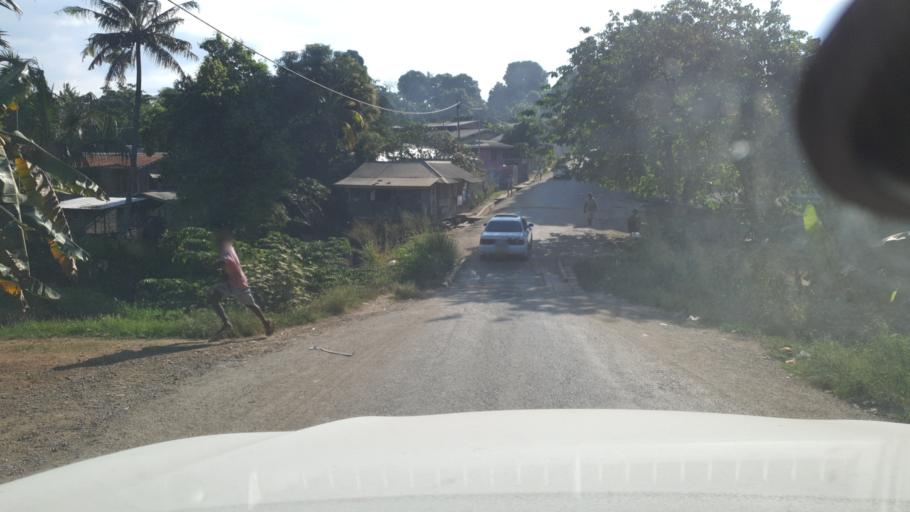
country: SB
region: Guadalcanal
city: Honiara
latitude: -9.4518
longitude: 159.9880
